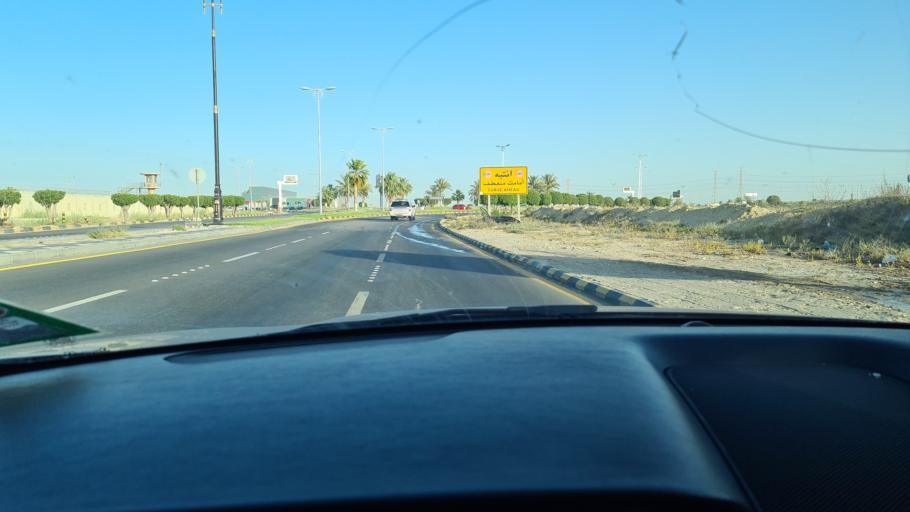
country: SA
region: Eastern Province
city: Al Jubayl
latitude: 26.9287
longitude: 49.7105
